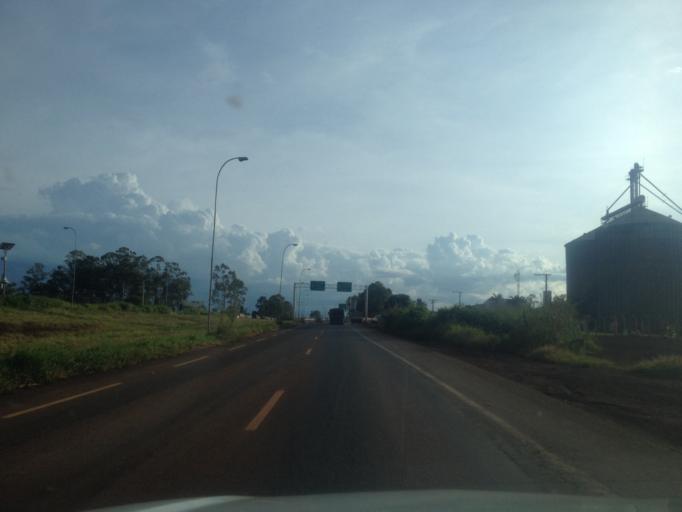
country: BR
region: Goias
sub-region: Jatai
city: Jatai
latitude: -17.9213
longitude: -51.7004
